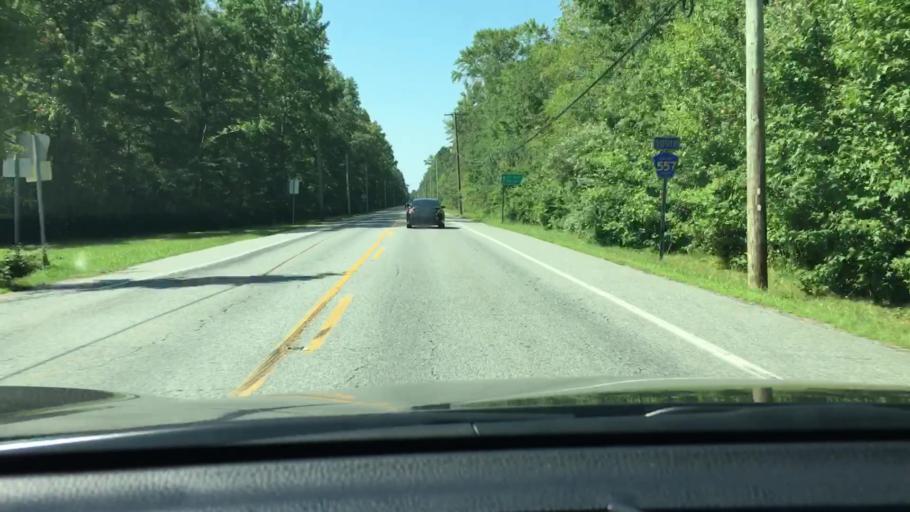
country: US
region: New Jersey
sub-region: Cape May County
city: Woodbine
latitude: 39.2949
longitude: -74.7818
